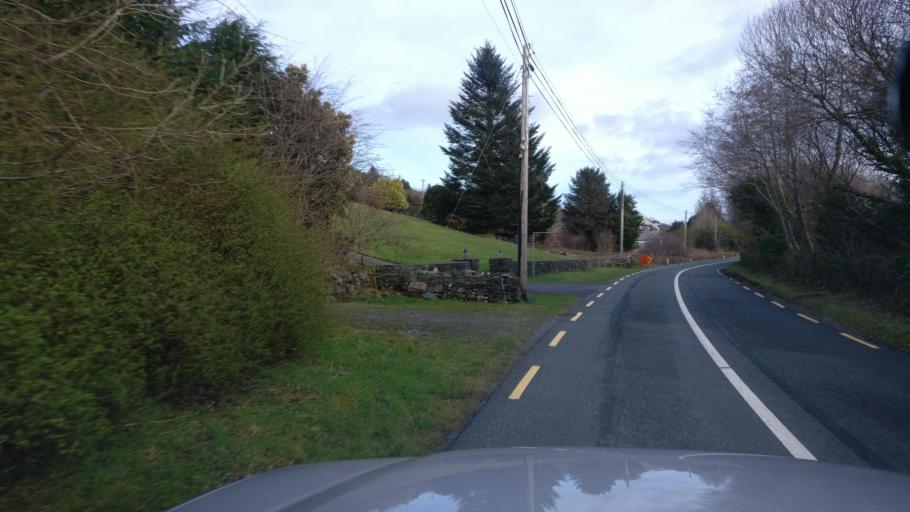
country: IE
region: Connaught
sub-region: County Galway
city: Oughterard
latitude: 53.5182
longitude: -9.4359
